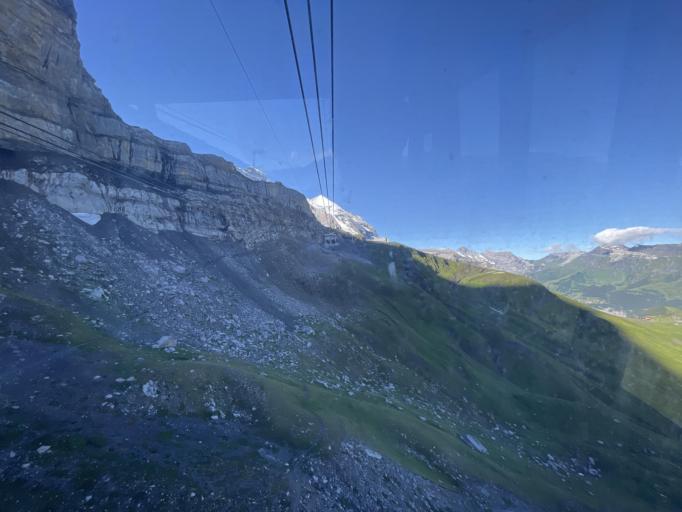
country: CH
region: Bern
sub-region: Interlaken-Oberhasli District
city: Grindelwald
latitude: 46.5797
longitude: 7.9794
